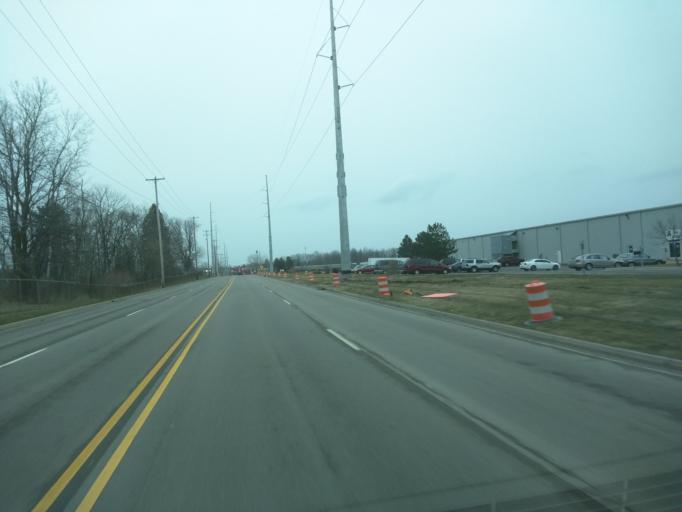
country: US
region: Michigan
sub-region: Eaton County
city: Waverly
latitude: 42.7121
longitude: -84.6159
